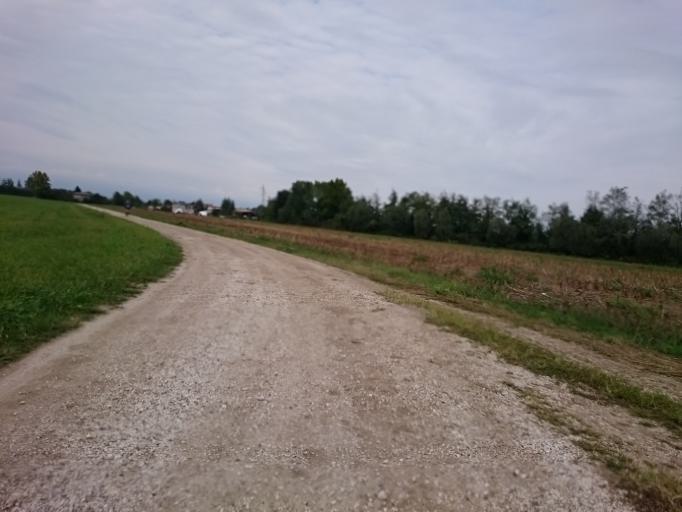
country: IT
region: Veneto
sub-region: Provincia di Vicenza
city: Quinto Vicentino
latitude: 45.5679
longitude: 11.6660
